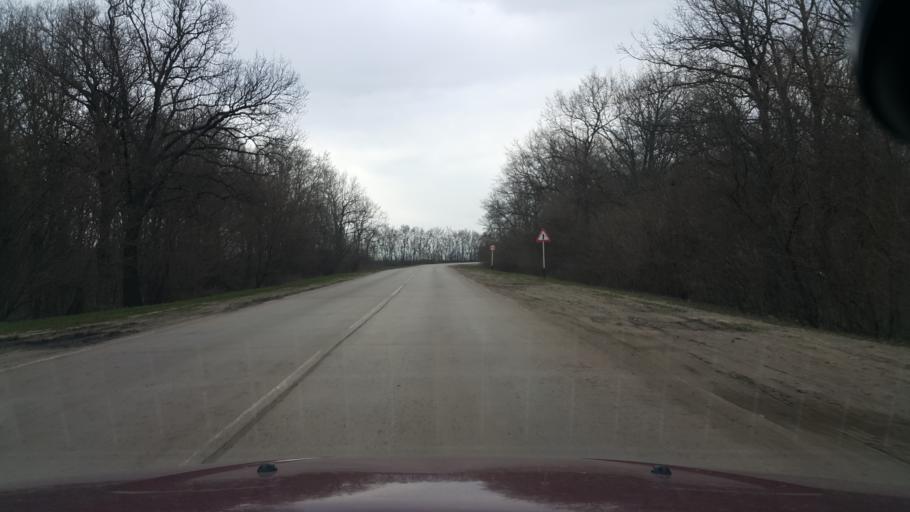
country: RU
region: Tambov
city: Bokino
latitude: 52.5612
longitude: 41.3565
